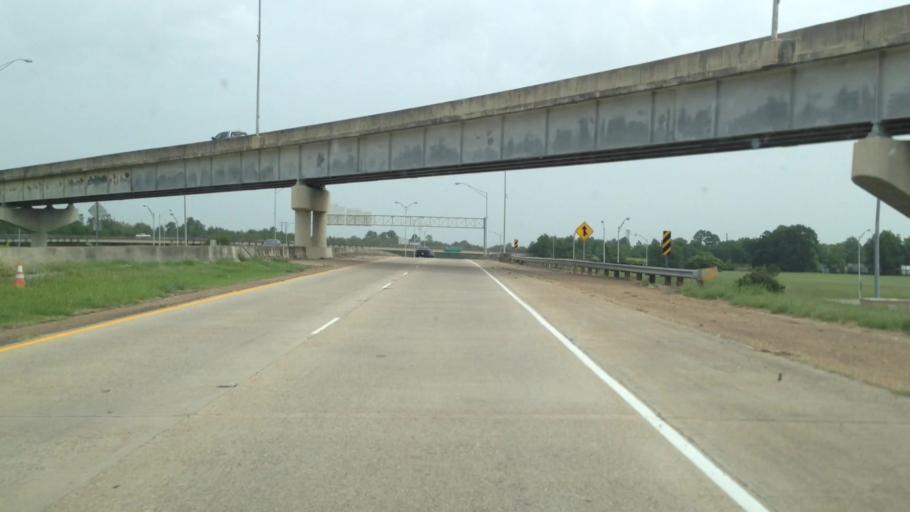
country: US
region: Louisiana
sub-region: Caddo Parish
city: Shreveport
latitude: 32.4551
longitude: -93.8439
